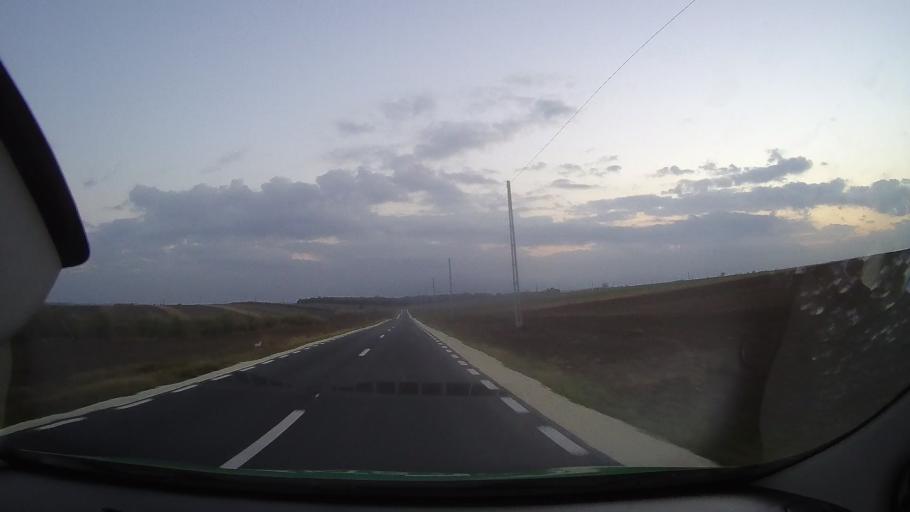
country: RO
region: Constanta
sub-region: Comuna Oltina
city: Oltina
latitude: 44.1208
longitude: 27.6671
